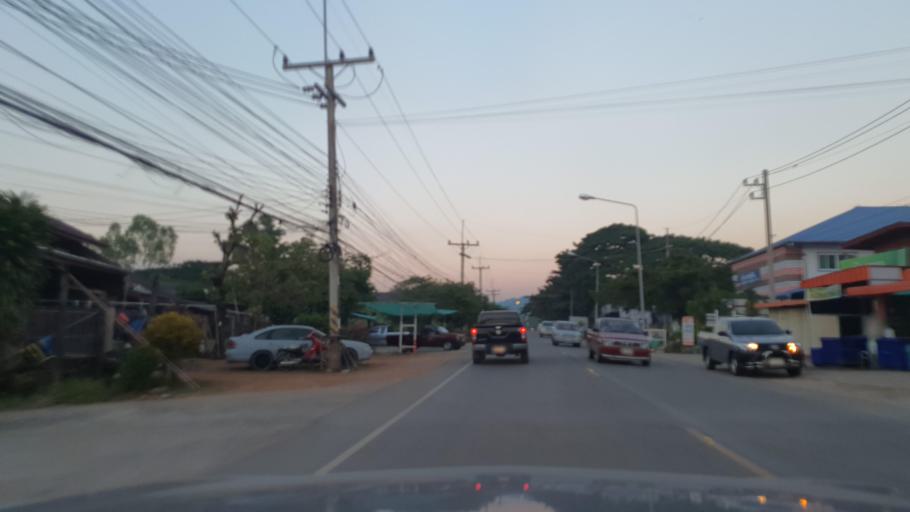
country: TH
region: Phayao
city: Dok Kham Tai
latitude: 19.0895
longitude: 100.0646
